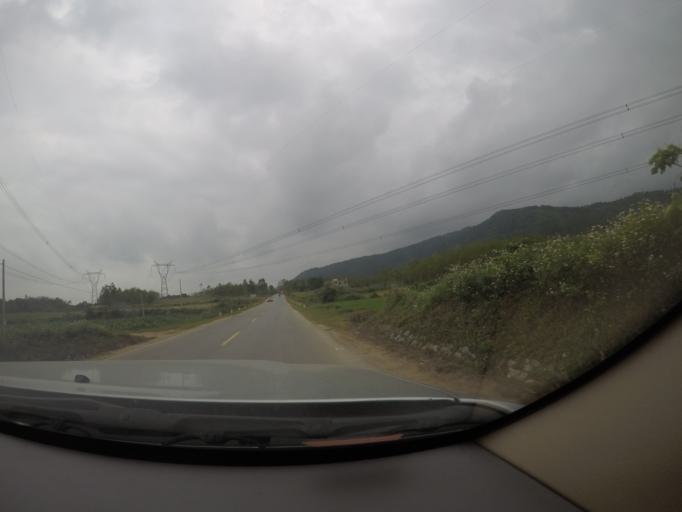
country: VN
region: Quang Binh
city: Hoan Lao
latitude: 17.5677
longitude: 106.4423
